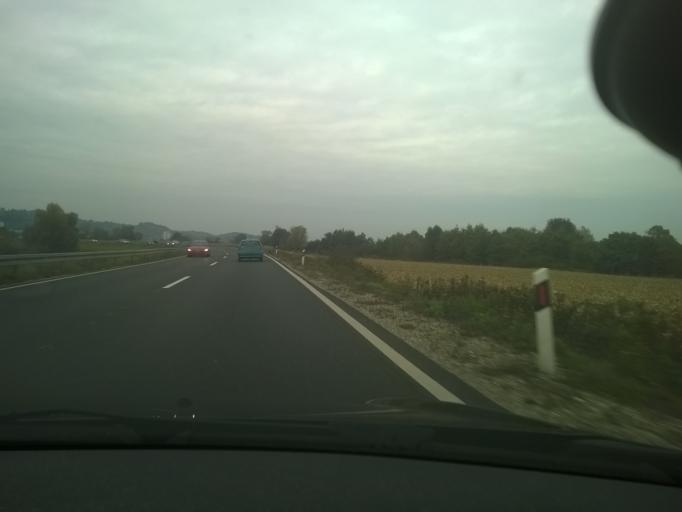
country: HR
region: Zagrebacka
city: Pojatno
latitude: 45.8991
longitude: 15.8162
